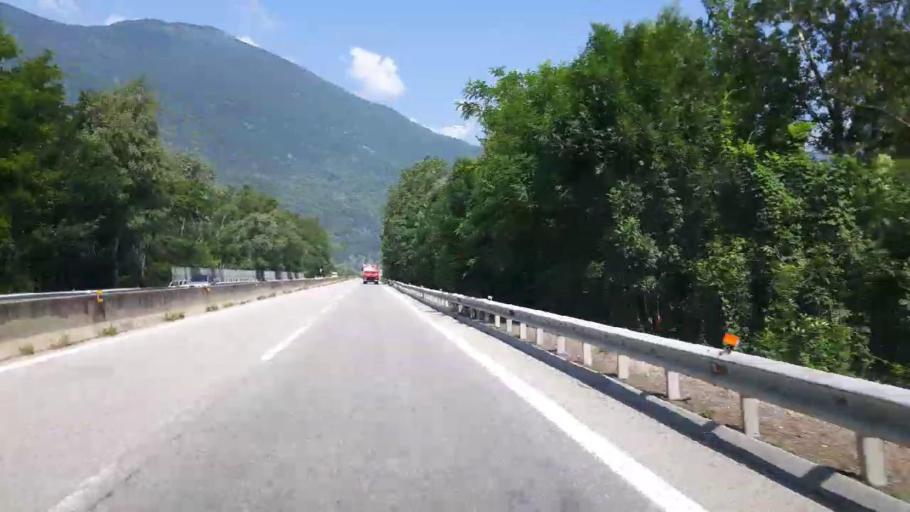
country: IT
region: Piedmont
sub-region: Provincia Verbano-Cusio-Ossola
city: Pallanzeno
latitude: 46.0344
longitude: 8.2741
